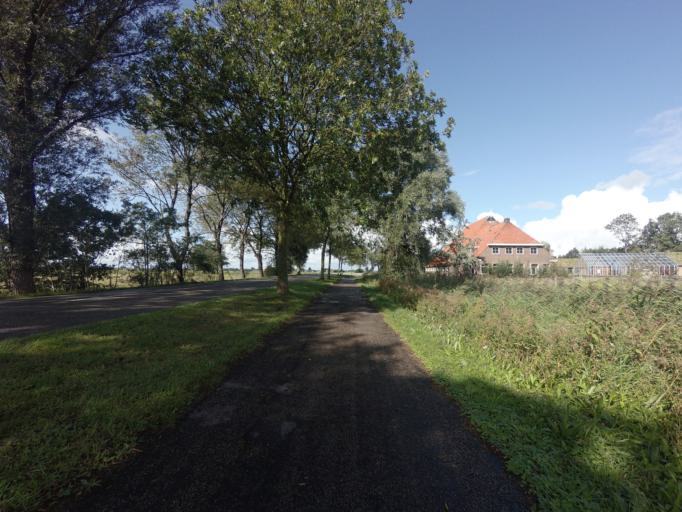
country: NL
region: Friesland
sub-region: Gemeente Boarnsterhim
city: Warten
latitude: 53.1502
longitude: 5.8780
